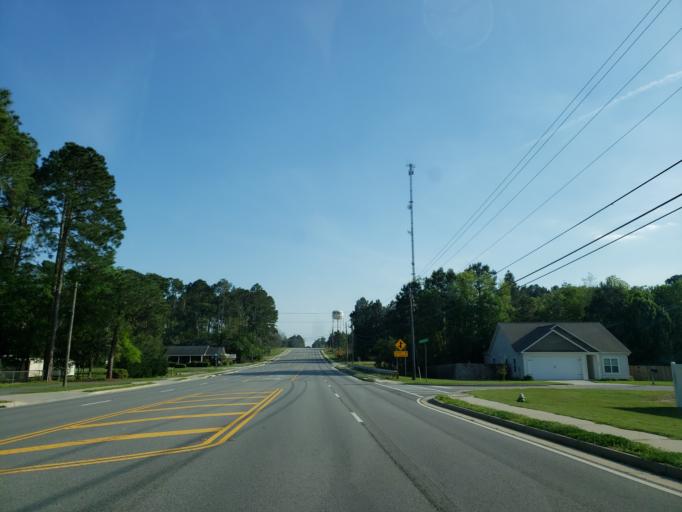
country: US
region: Georgia
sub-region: Tift County
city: Tifton
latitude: 31.4784
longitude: -83.5429
